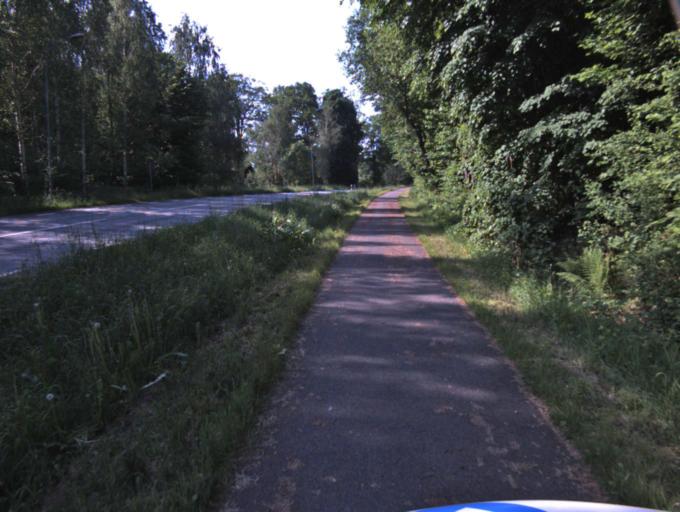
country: SE
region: Skane
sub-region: Kristianstads Kommun
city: Tollarp
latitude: 56.1682
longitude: 14.2819
